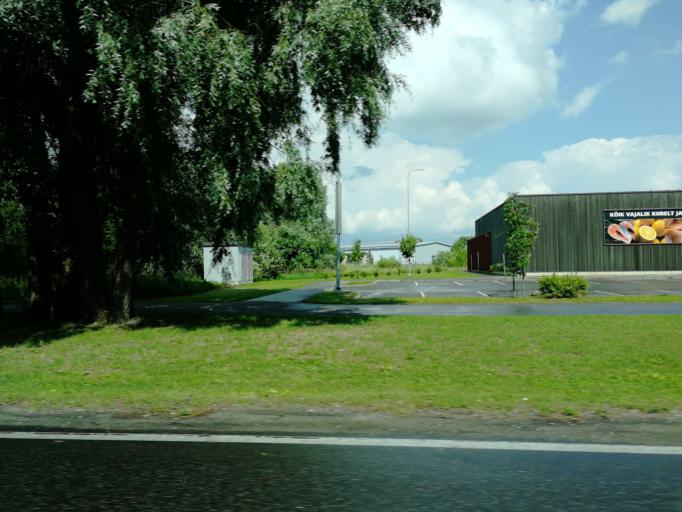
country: EE
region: Paernumaa
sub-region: Paernu linn
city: Parnu
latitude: 58.3938
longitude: 24.4602
